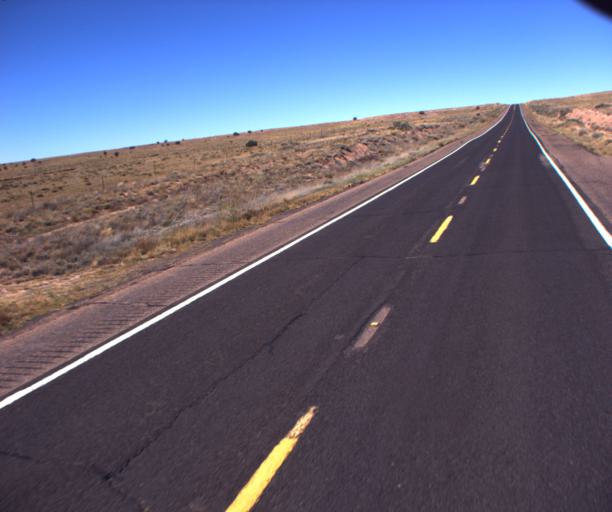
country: US
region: Arizona
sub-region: Navajo County
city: Snowflake
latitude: 34.6971
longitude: -109.7500
